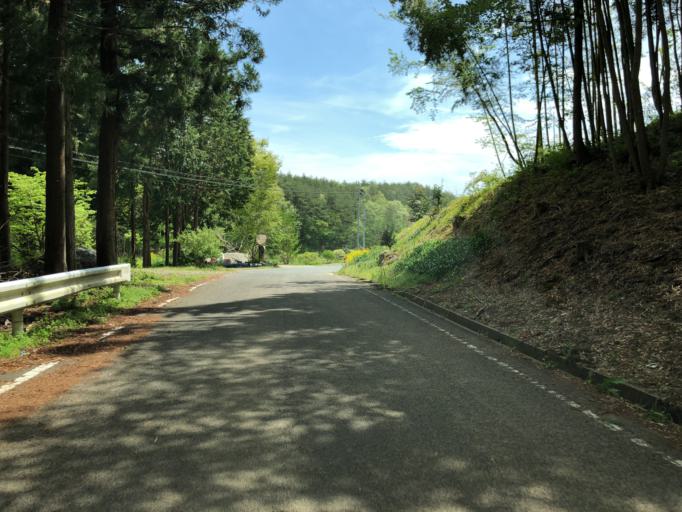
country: JP
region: Miyagi
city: Marumori
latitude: 37.7002
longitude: 140.7787
